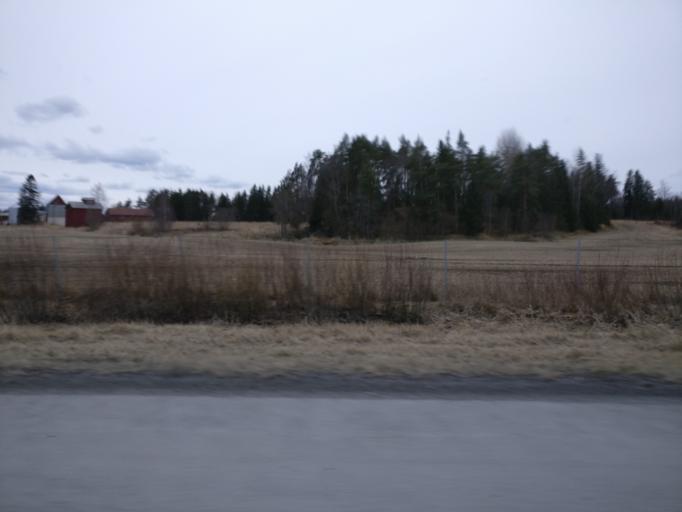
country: FI
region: Pirkanmaa
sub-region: Etelae-Pirkanmaa
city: Akaa
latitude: 61.1712
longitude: 23.9326
